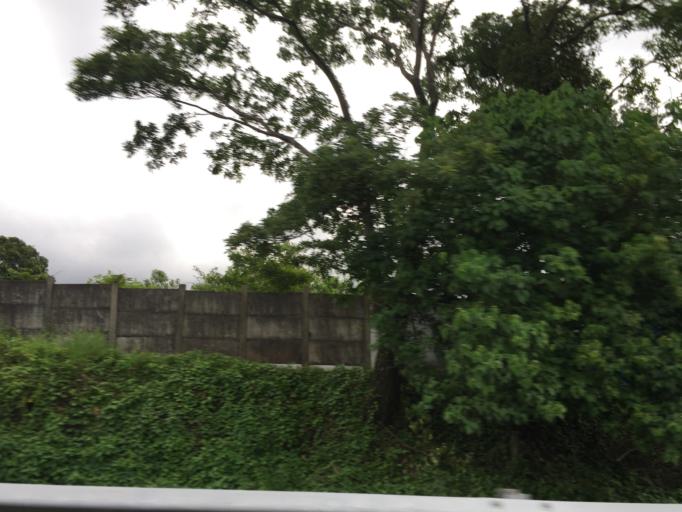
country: GT
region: Escuintla
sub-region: Municipio de Escuintla
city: Escuintla
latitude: 14.3793
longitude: -90.8205
